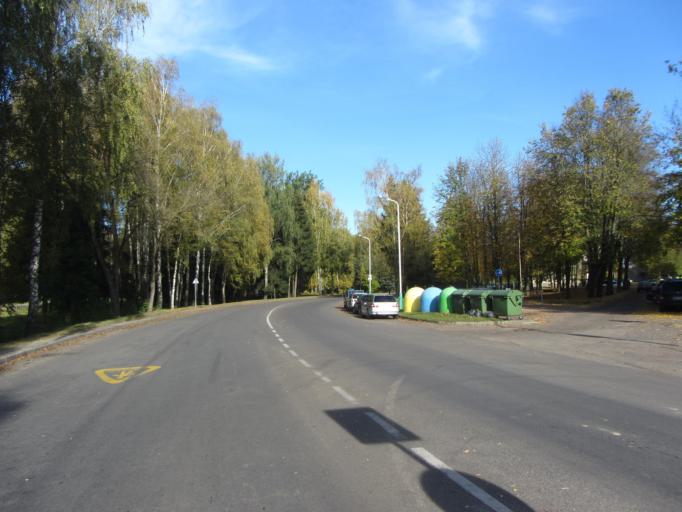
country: LT
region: Vilnius County
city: Elektrenai
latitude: 54.7887
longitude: 24.6599
